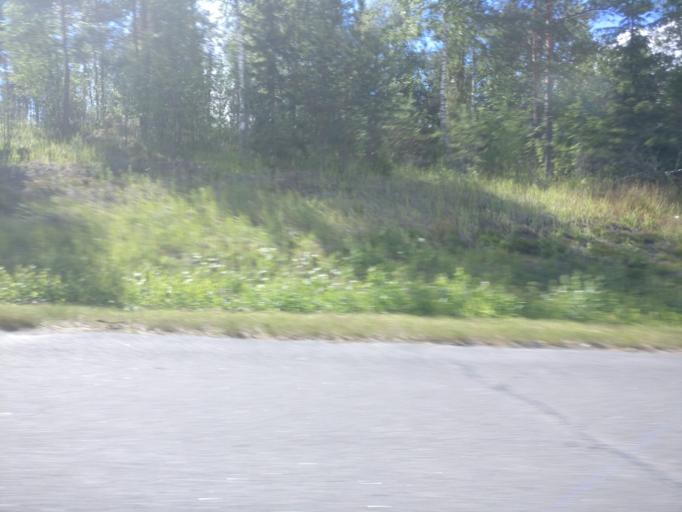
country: FI
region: Paijanne Tavastia
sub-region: Lahti
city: Heinola
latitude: 61.3235
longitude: 26.0418
